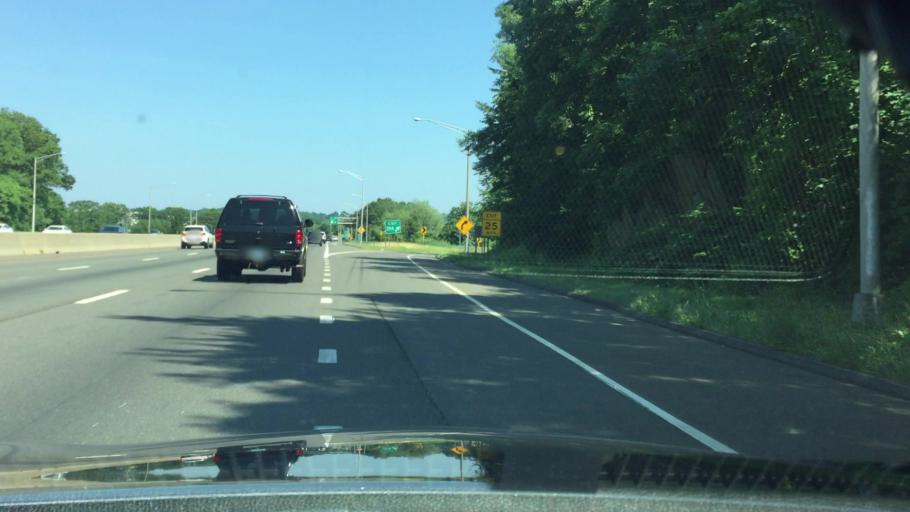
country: US
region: Connecticut
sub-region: New Haven County
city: Milford
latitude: 41.2353
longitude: -73.0461
